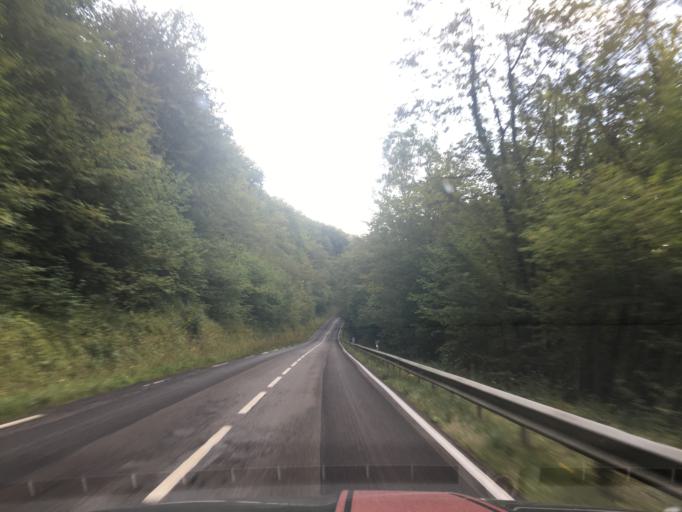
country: FR
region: Lorraine
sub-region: Departement de Meurthe-et-Moselle
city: Saulnes
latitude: 49.5157
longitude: 5.8436
